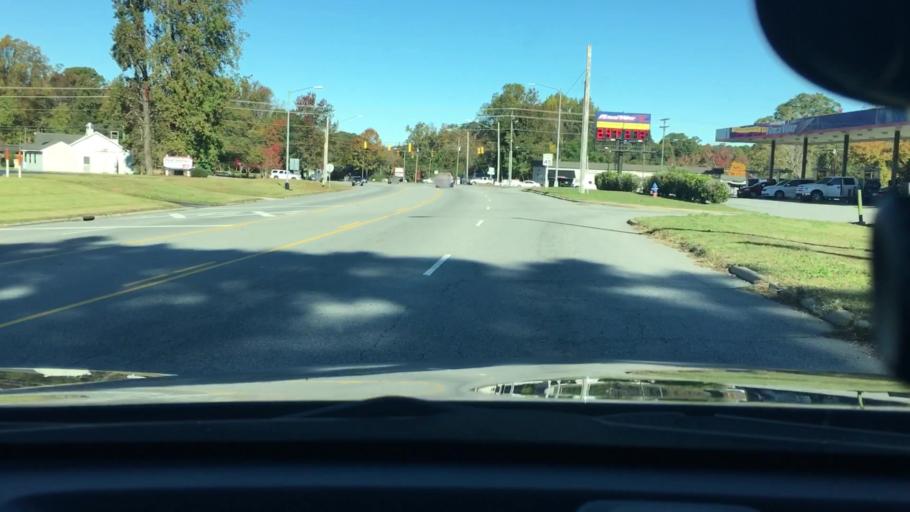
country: US
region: North Carolina
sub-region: Edgecombe County
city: Tarboro
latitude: 35.8901
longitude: -77.5484
